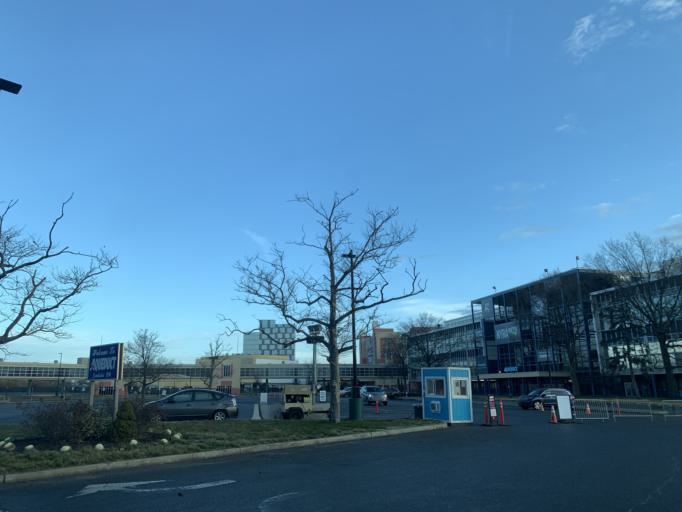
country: US
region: New York
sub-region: Queens County
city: Borough of Queens
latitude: 40.6709
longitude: -73.8349
